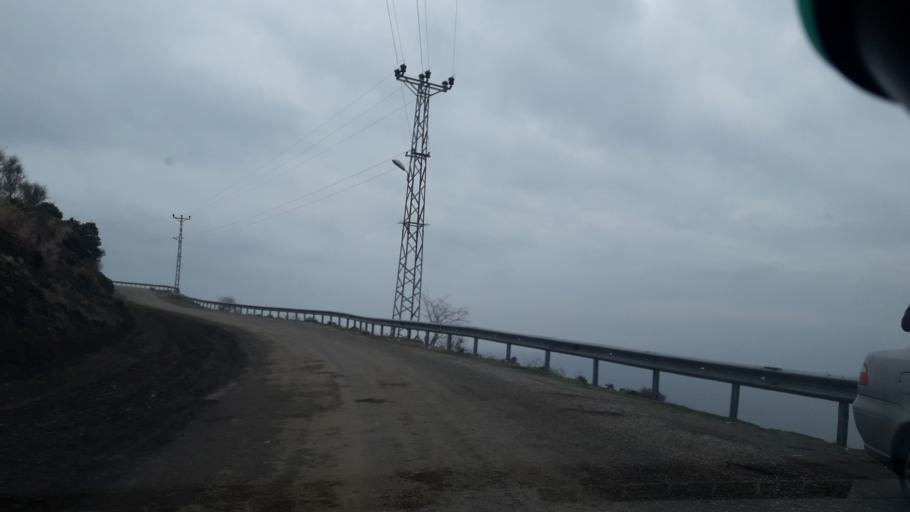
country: TR
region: Sinop
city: Sinop
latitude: 42.0169
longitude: 35.2022
